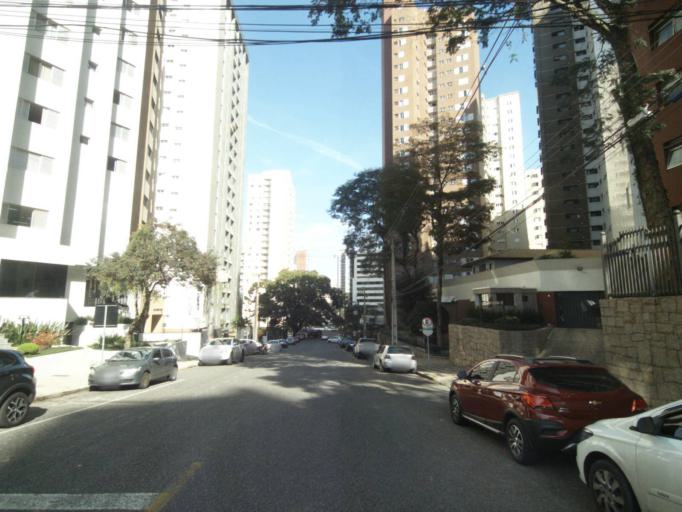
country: BR
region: Parana
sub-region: Curitiba
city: Curitiba
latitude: -25.4463
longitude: -49.2881
